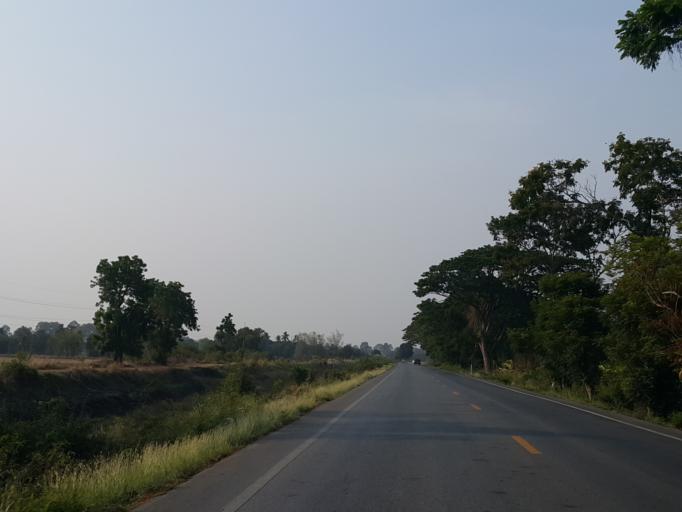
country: TH
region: Chai Nat
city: Sankhaburi
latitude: 15.0275
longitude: 100.1447
